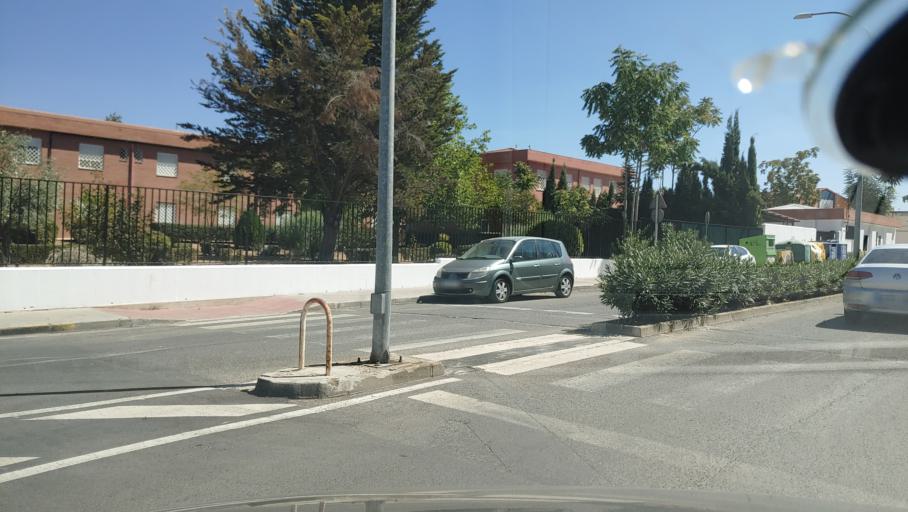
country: ES
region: Castille-La Mancha
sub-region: Provincia de Ciudad Real
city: Valdepenas
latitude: 38.7709
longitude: -3.3832
